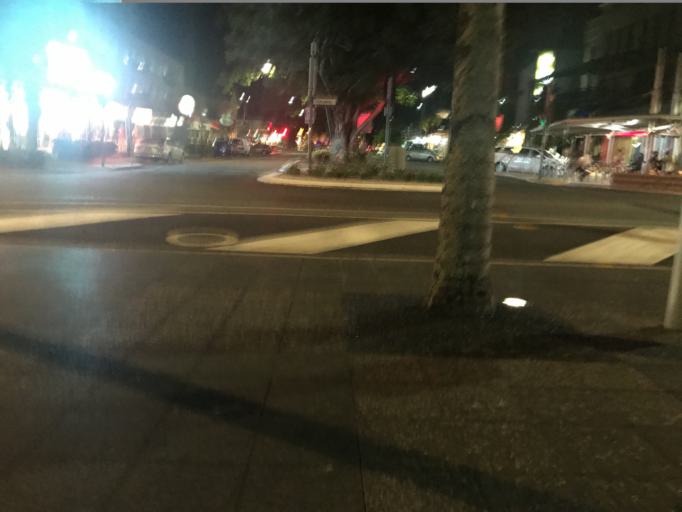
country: AU
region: Queensland
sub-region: Cairns
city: Cairns
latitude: -16.9205
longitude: 145.7779
